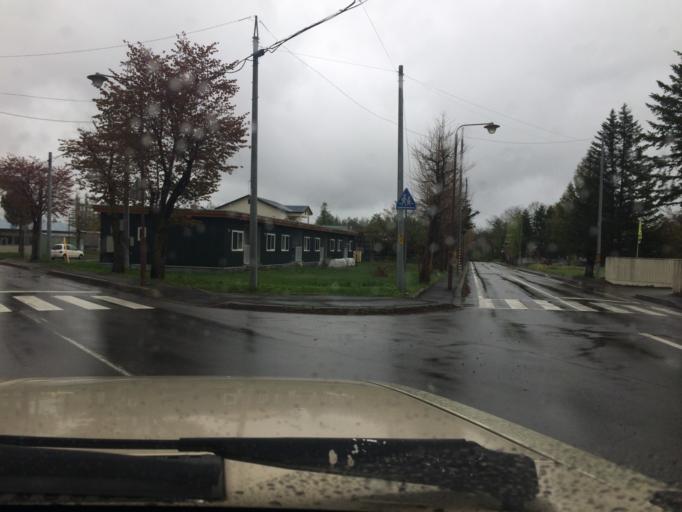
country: JP
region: Hokkaido
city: Obihiro
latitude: 42.8042
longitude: 142.9547
